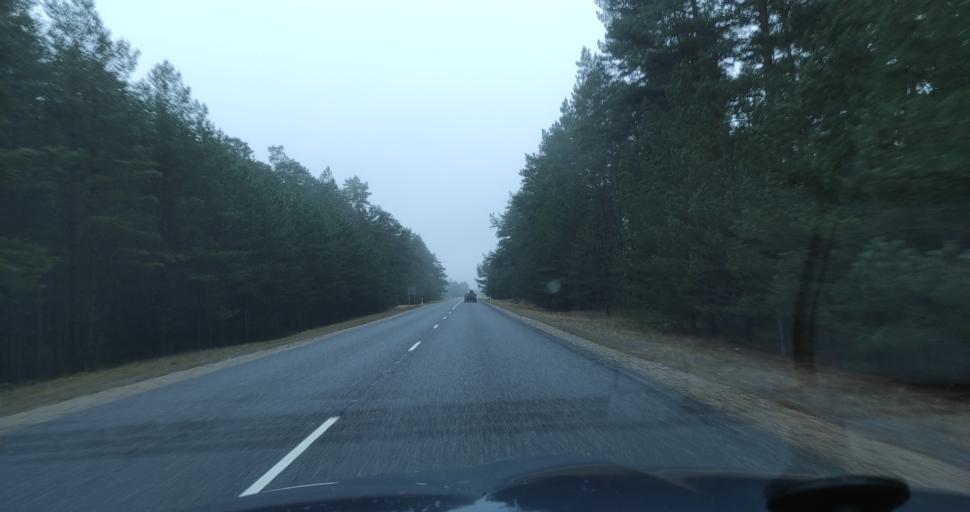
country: LV
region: Pavilostas
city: Pavilosta
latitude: 56.9676
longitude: 21.3407
